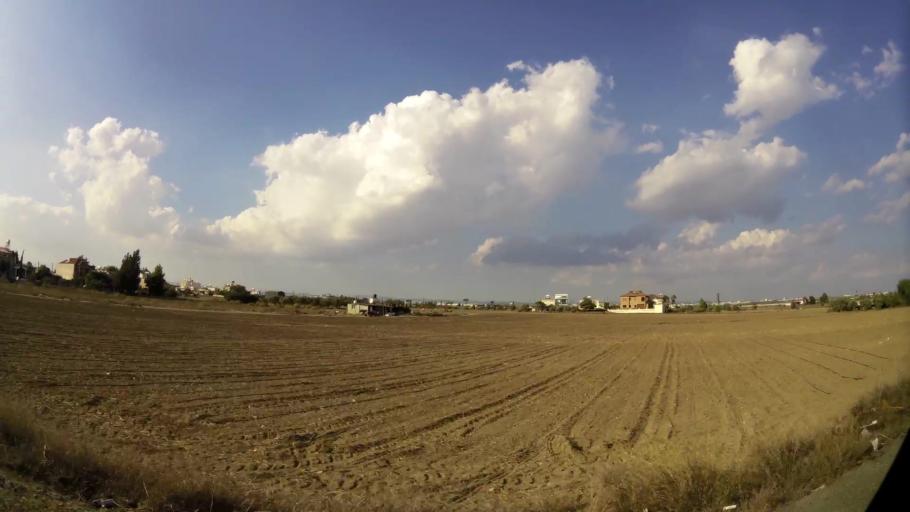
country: CY
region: Larnaka
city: Dhromolaxia
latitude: 34.8735
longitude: 33.5969
